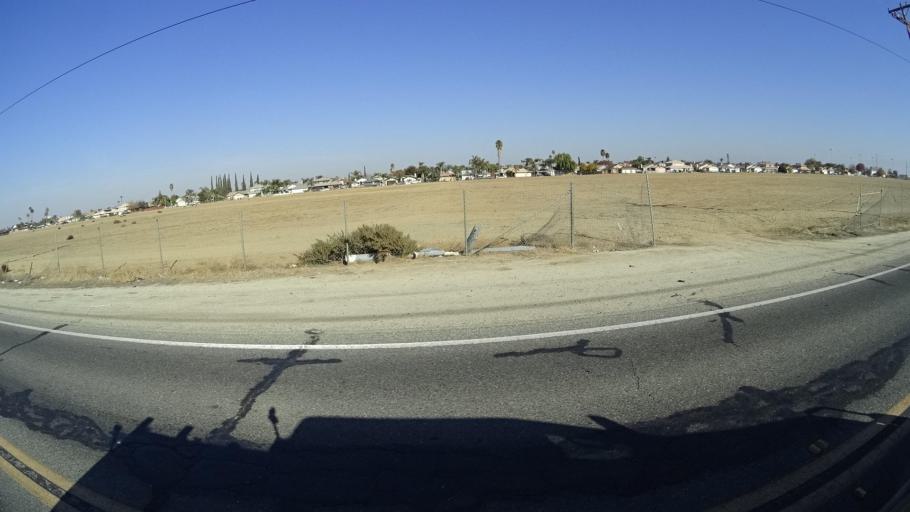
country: US
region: California
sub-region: Kern County
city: Delano
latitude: 35.7616
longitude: -119.2279
